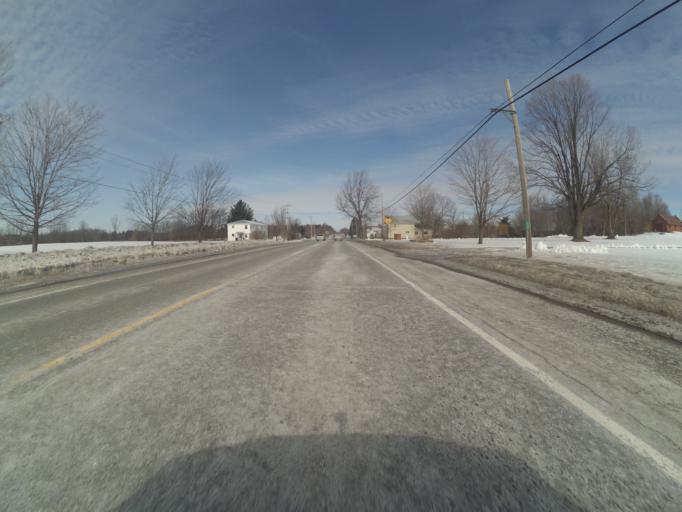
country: US
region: New York
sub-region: St. Lawrence County
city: Potsdam
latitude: 44.6546
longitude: -74.9720
